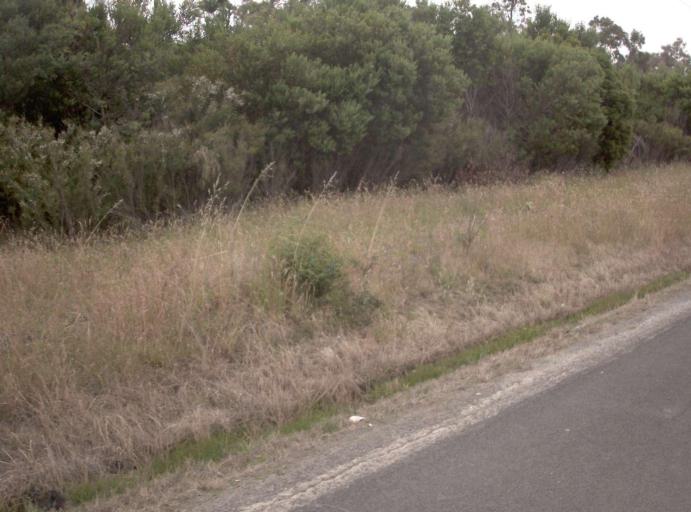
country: AU
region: Victoria
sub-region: Latrobe
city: Traralgon
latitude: -38.2160
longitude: 146.4792
